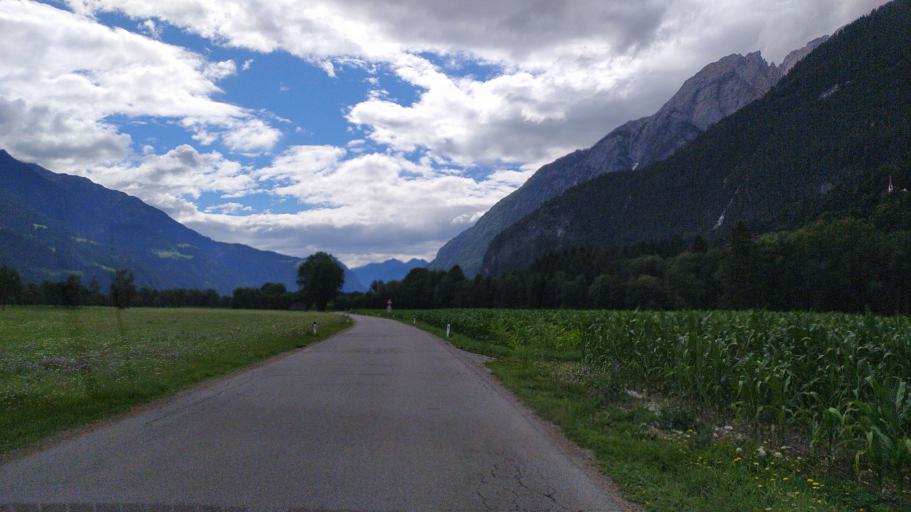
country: AT
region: Tyrol
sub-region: Politischer Bezirk Lienz
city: Lavant
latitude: 46.8030
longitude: 12.8324
